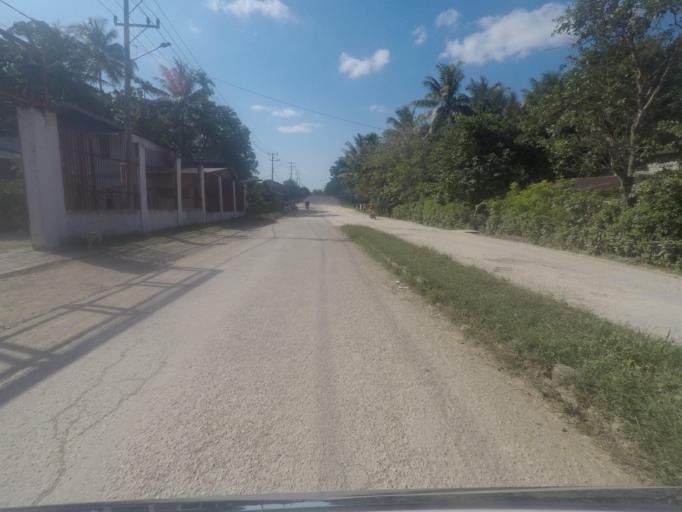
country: TL
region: Lautem
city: Lospalos
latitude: -8.5127
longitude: 127.0043
